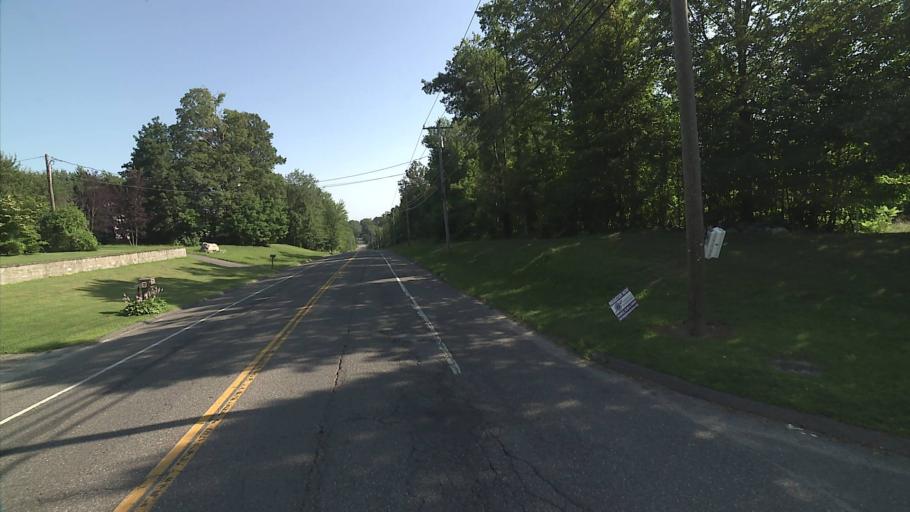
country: US
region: Connecticut
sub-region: Litchfield County
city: Torrington
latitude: 41.8373
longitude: -73.0765
